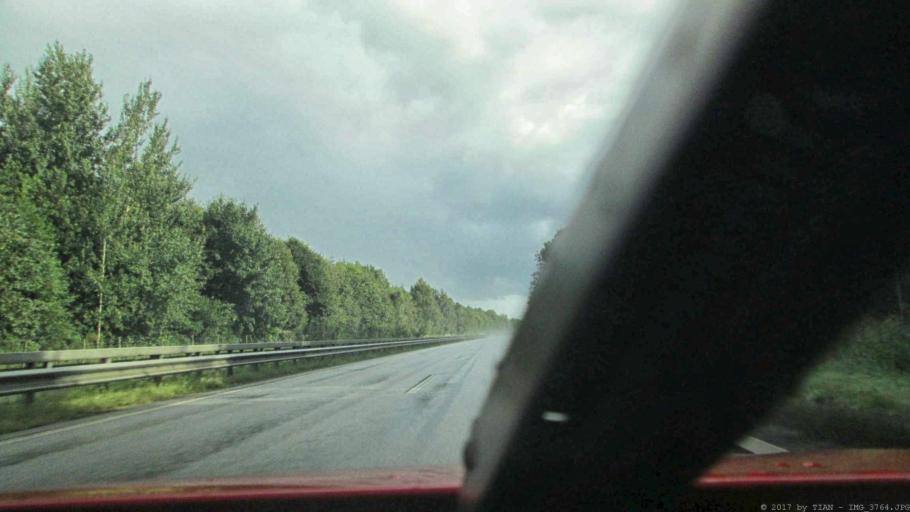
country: DE
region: Schleswig-Holstein
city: Ottenbuttel
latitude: 53.9851
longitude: 9.4907
